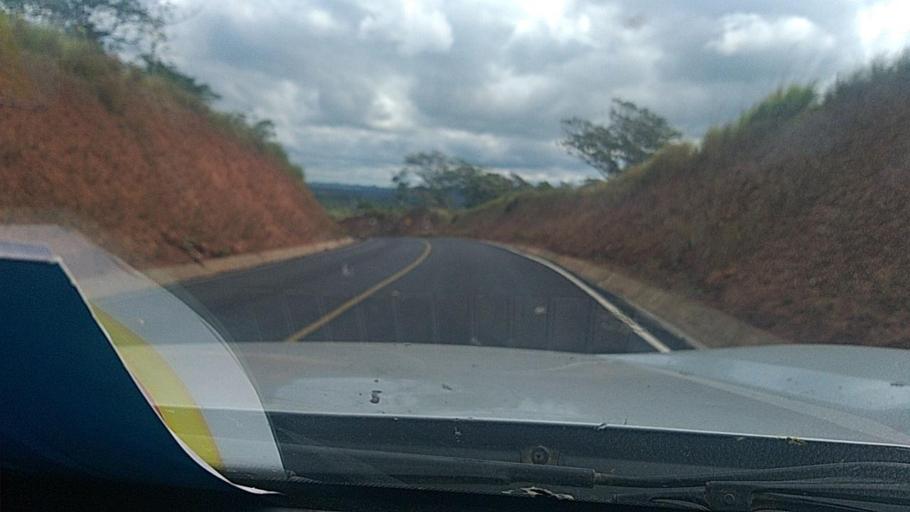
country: NI
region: Atlantico Sur
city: Muelle de los Bueyes
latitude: 12.1292
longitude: -84.4343
